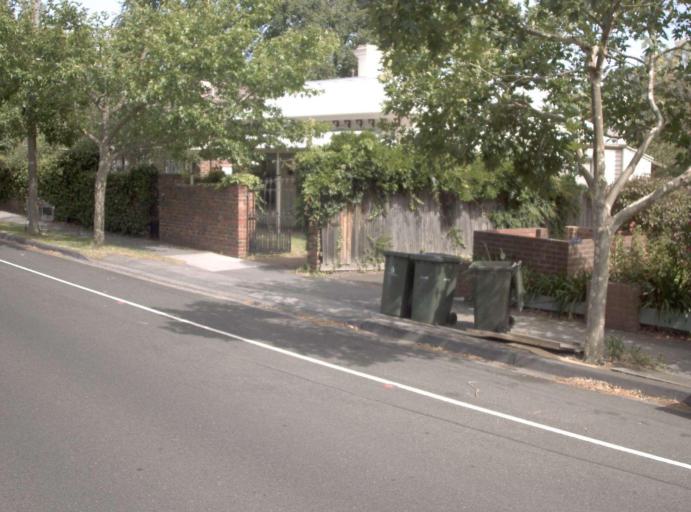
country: AU
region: Victoria
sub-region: Boroondara
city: Hawthorn East
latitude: -37.8206
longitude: 145.0523
